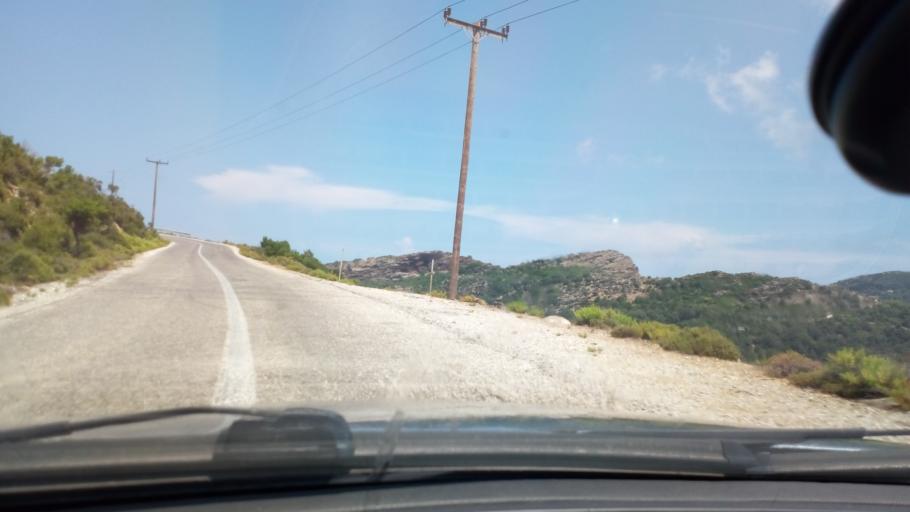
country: GR
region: North Aegean
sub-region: Nomos Samou
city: Agios Kirykos
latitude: 37.6386
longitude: 26.2543
